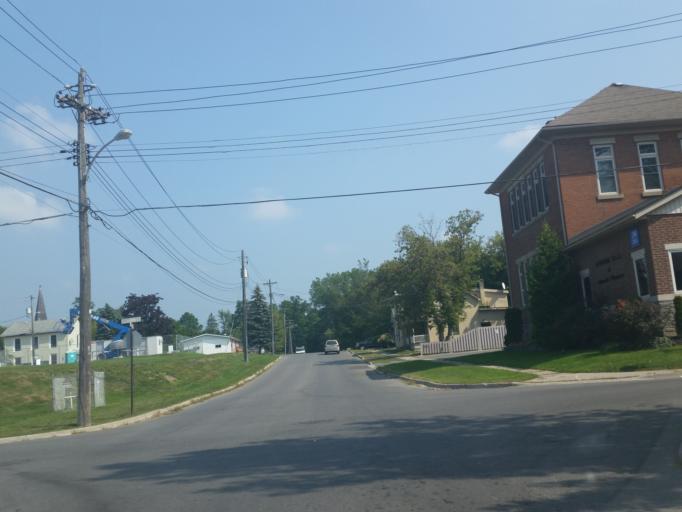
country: CA
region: Ontario
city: Picton
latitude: 44.0065
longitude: -77.1353
